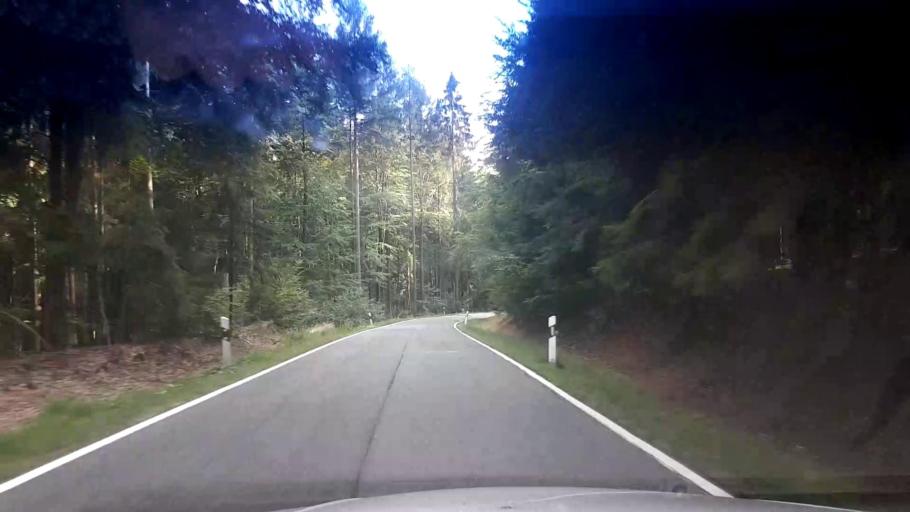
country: DE
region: Bavaria
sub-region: Upper Palatinate
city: Neualbenreuth
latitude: 49.9345
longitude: 12.4089
